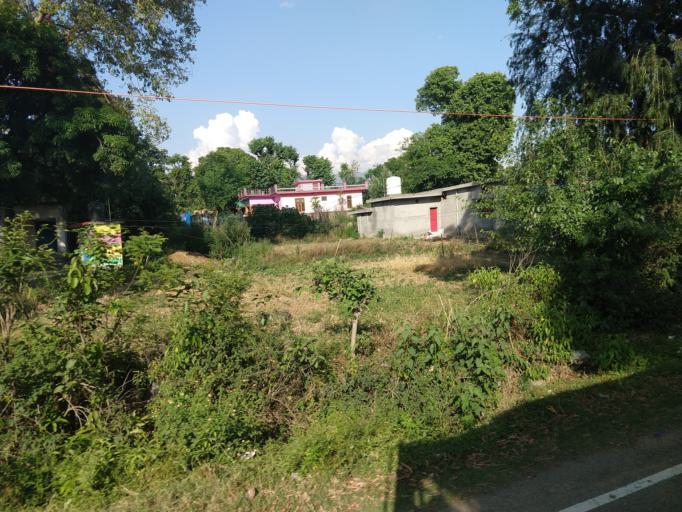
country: IN
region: Himachal Pradesh
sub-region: Chamba
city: Chowari
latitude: 32.3612
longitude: 75.9207
